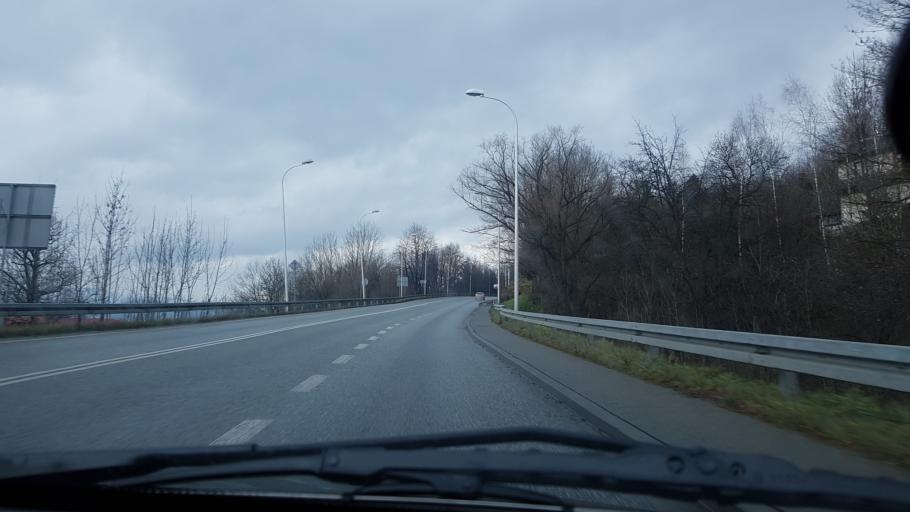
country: PL
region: Silesian Voivodeship
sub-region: Powiat zywiecki
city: Zywiec
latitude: 49.7006
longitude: 19.2021
